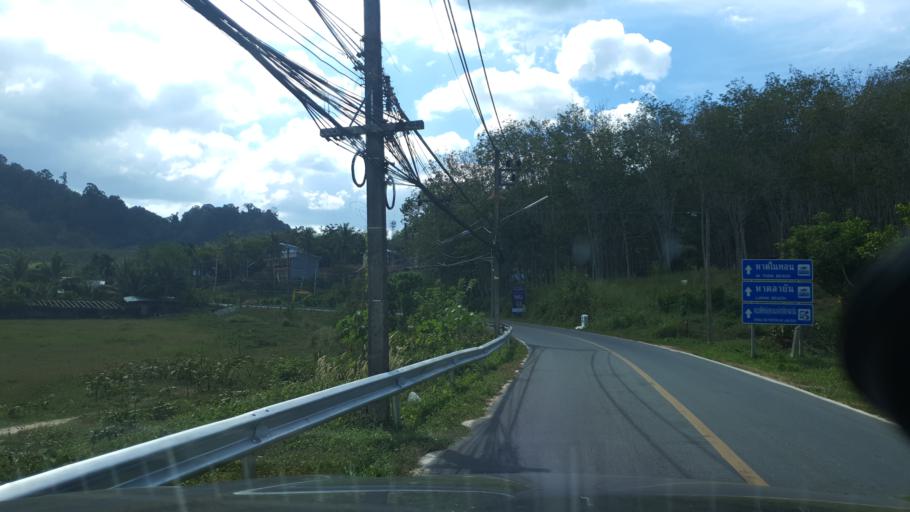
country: TH
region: Phuket
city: Thalang
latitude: 8.0695
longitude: 98.2945
